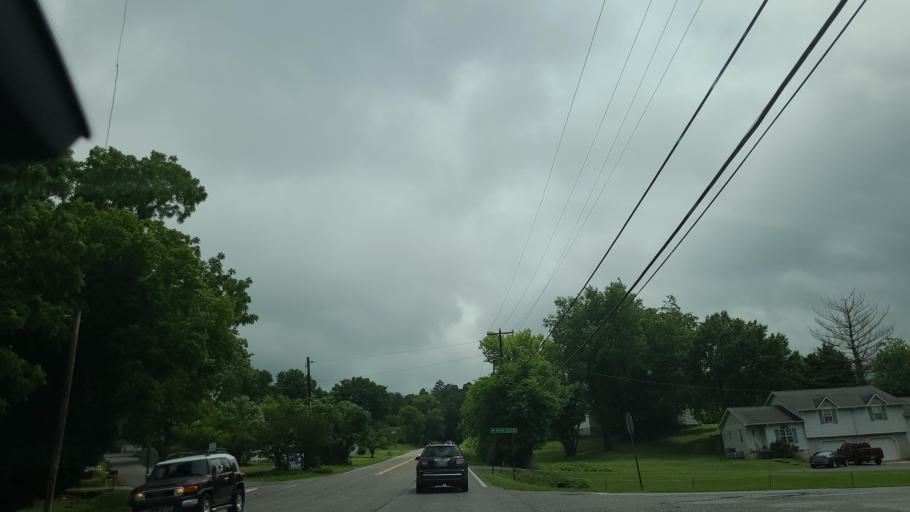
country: US
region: Tennessee
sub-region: Rhea County
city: Dayton
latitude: 35.4936
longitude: -85.0060
